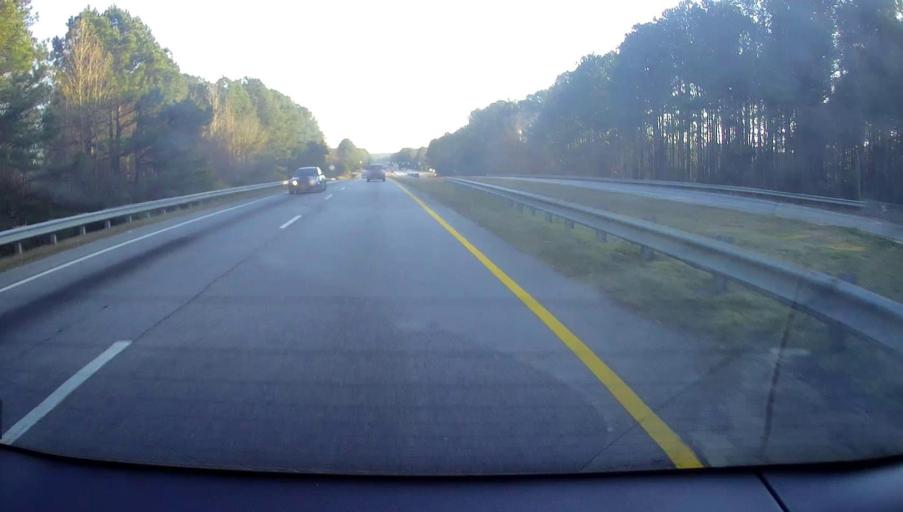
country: US
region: Georgia
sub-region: Fayette County
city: Tyrone
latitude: 33.4822
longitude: -84.5855
